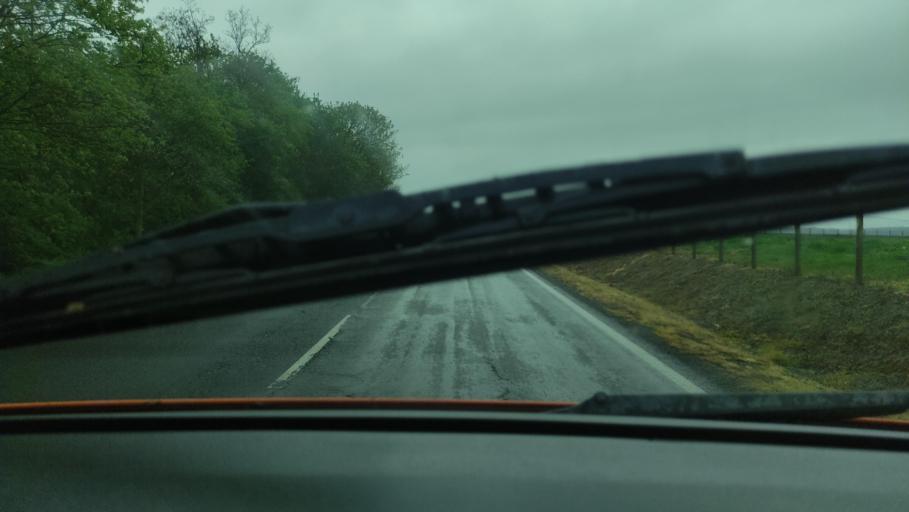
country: HU
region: Baranya
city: Mohacs
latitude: 45.9288
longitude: 18.6598
